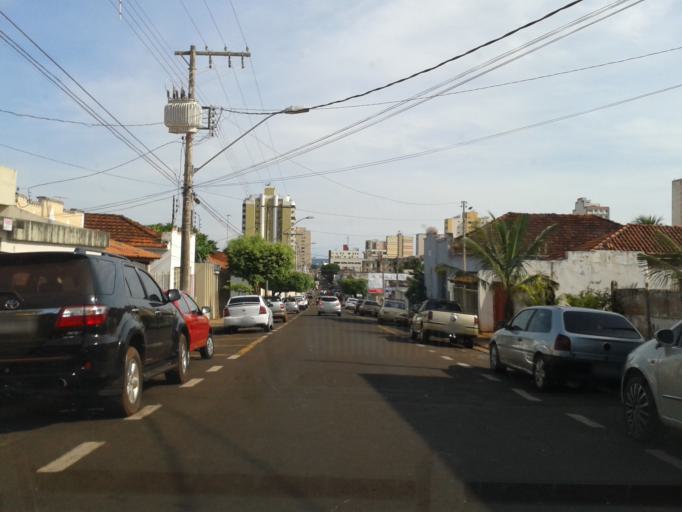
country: BR
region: Minas Gerais
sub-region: Ituiutaba
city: Ituiutaba
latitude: -18.9778
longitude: -49.4639
